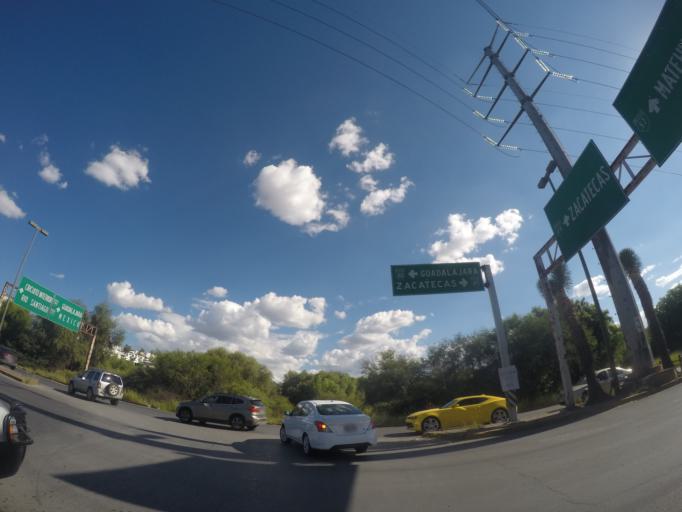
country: MX
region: San Luis Potosi
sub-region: Mexquitic de Carmona
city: Guadalupe Victoria
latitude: 22.1521
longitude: -101.0317
